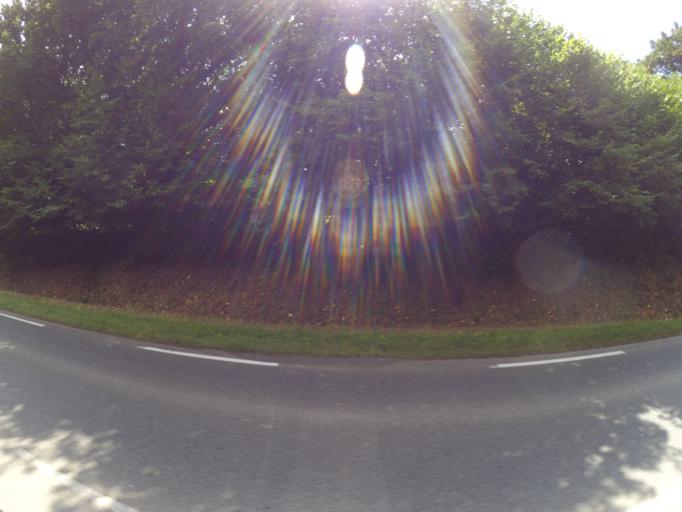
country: FR
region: Brittany
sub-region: Departement du Finistere
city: Elliant
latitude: 47.9690
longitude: -3.9040
